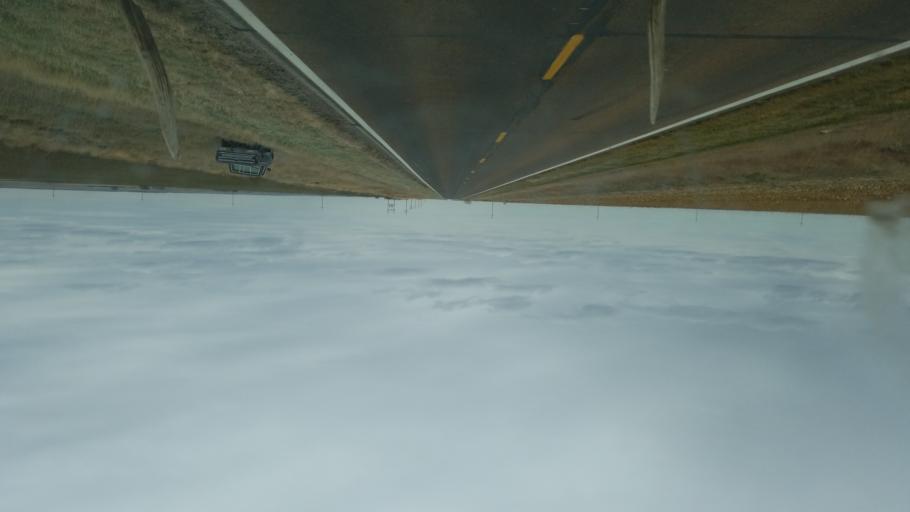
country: US
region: Kansas
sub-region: Wallace County
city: Sharon Springs
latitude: 38.9020
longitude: -101.7280
